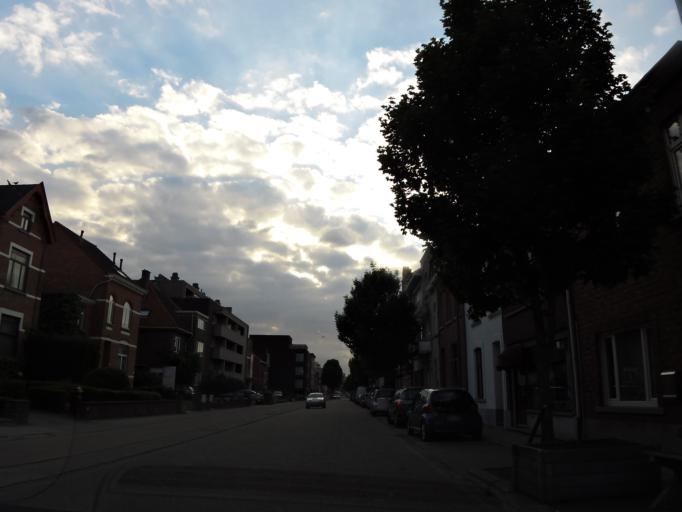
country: BE
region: Flanders
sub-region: Provincie Limburg
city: Hasselt
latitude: 50.9290
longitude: 5.3530
